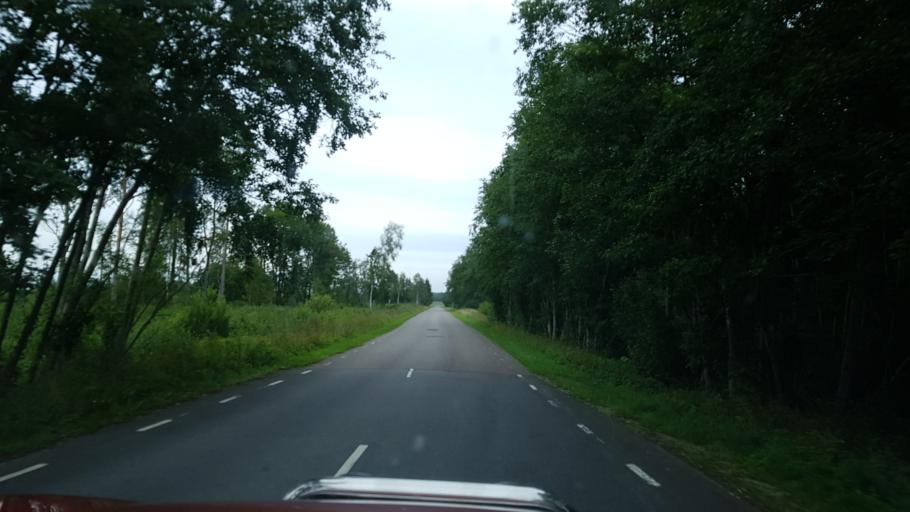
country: EE
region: Laeaene
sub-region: Lihula vald
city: Lihula
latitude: 58.8790
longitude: 23.8216
